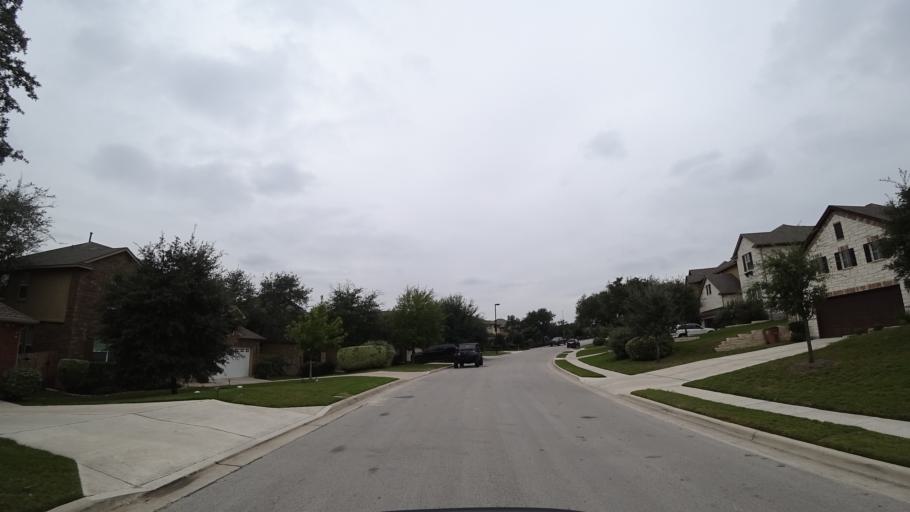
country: US
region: Texas
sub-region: Travis County
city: Shady Hollow
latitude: 30.1796
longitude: -97.8996
